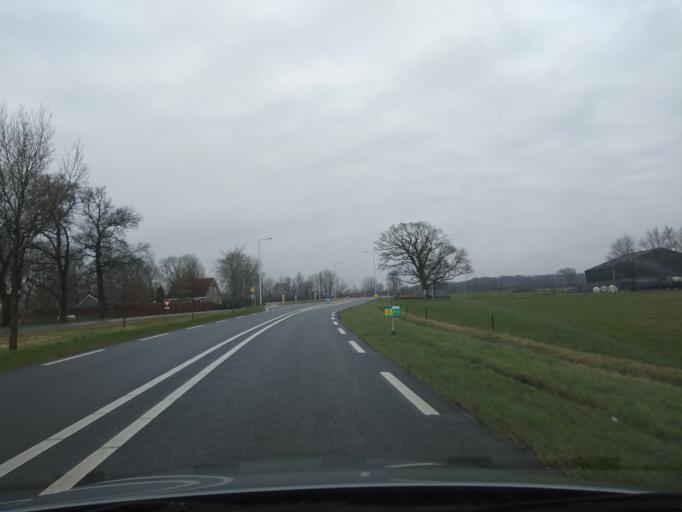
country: NL
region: Overijssel
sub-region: Gemeente Steenwijkerland
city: Sint Jansklooster
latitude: 52.6618
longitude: 5.9924
